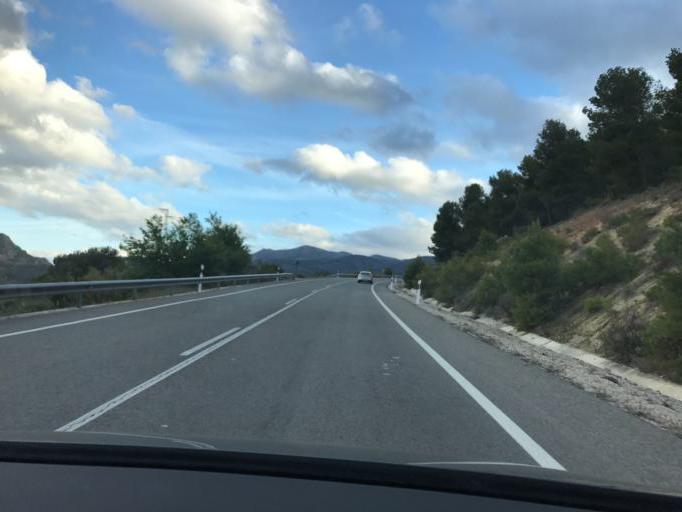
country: ES
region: Andalusia
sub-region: Provincia de Jaen
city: Belmez de la Moraleda
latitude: 37.7644
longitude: -3.3335
